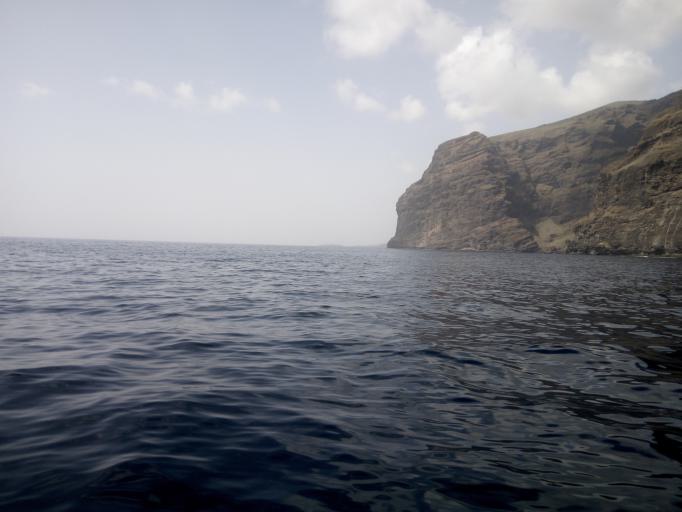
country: ES
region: Canary Islands
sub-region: Provincia de Santa Cruz de Tenerife
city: Santiago del Teide
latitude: 28.2857
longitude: -16.8662
